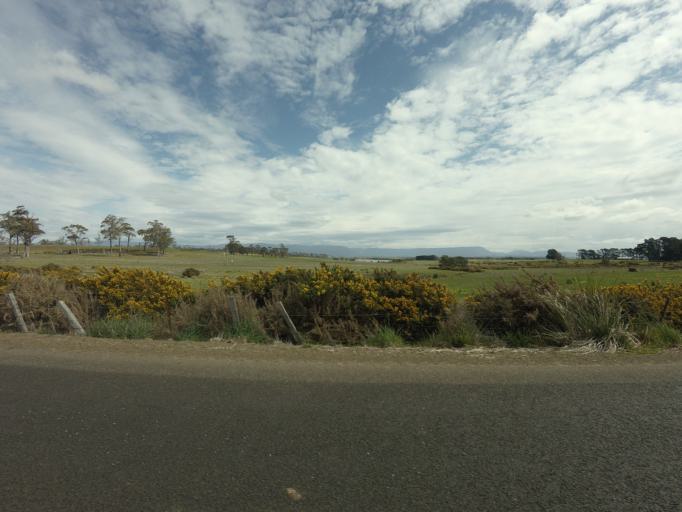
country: AU
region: Tasmania
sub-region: Northern Midlands
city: Longford
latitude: -41.7210
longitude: 147.1886
